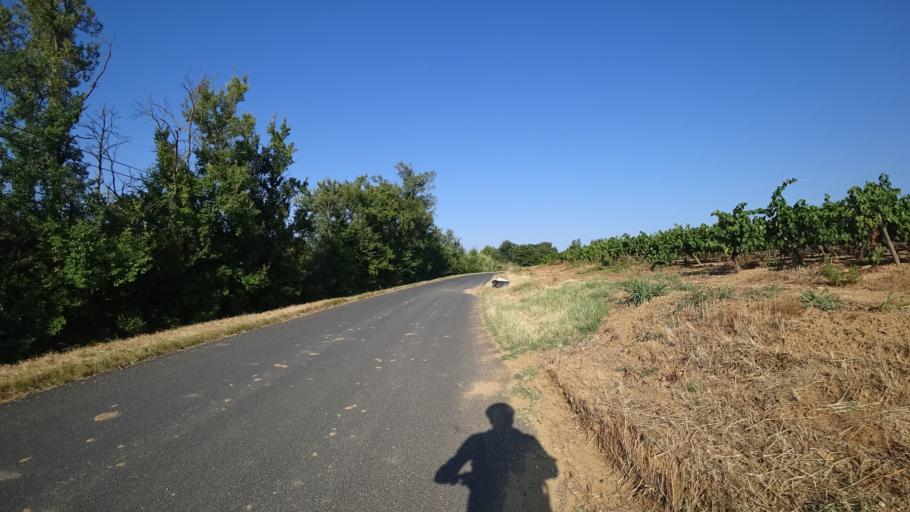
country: FR
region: Languedoc-Roussillon
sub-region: Departement des Pyrenees-Orientales
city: Villelongue-de-la-Salanque
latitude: 42.6975
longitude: 2.9862
